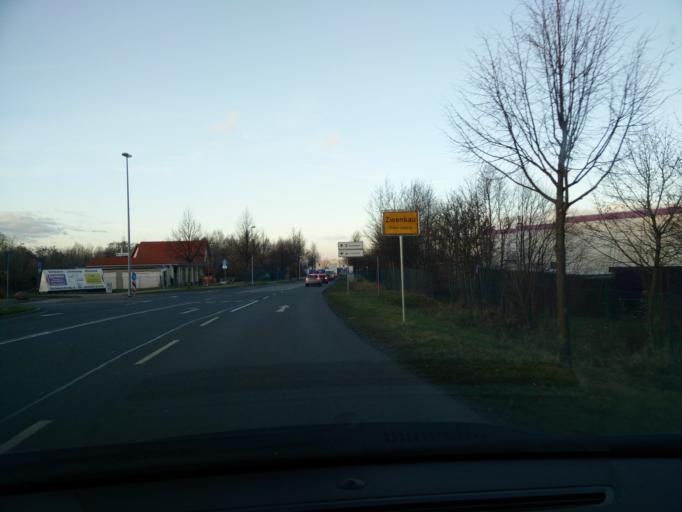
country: DE
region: Saxony
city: Zwenkau
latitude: 51.2134
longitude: 12.3439
